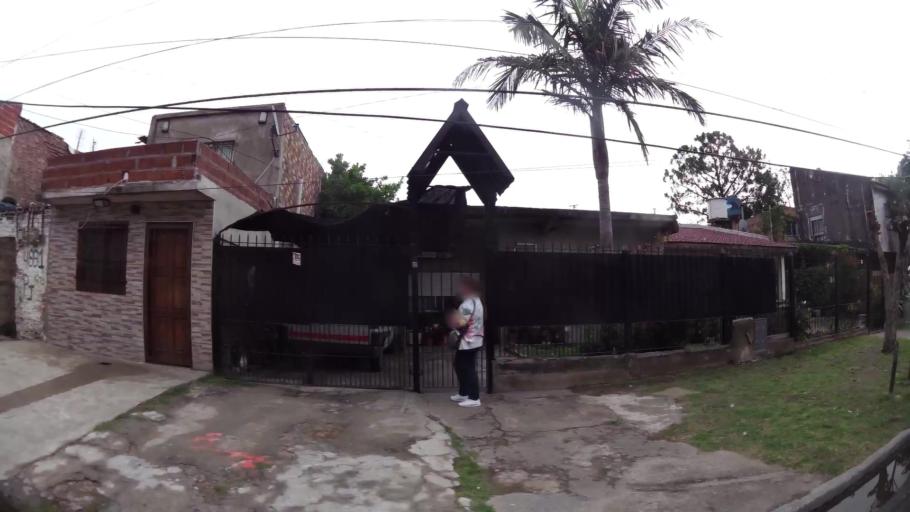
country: AR
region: Buenos Aires
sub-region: Partido de Lanus
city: Lanus
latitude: -34.7277
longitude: -58.3445
